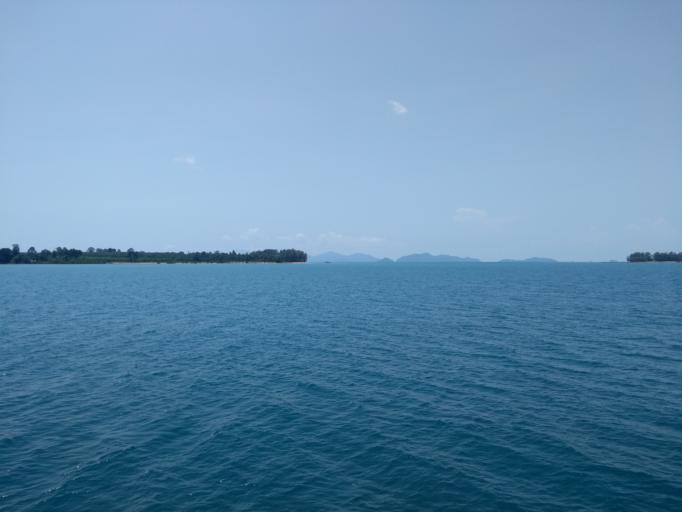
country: TH
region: Trat
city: Ko Kut
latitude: 11.8139
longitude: 102.5196
